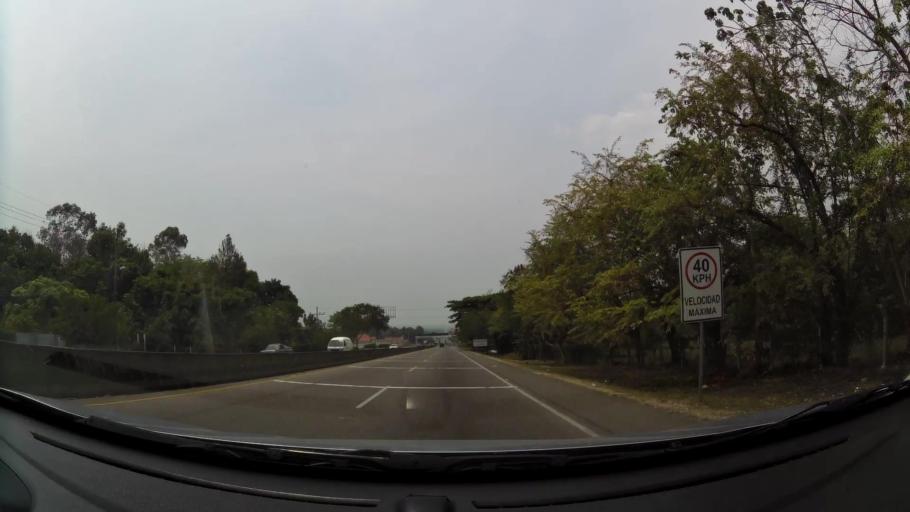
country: HN
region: Cortes
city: Oropendolas
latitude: 15.0275
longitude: -87.9277
